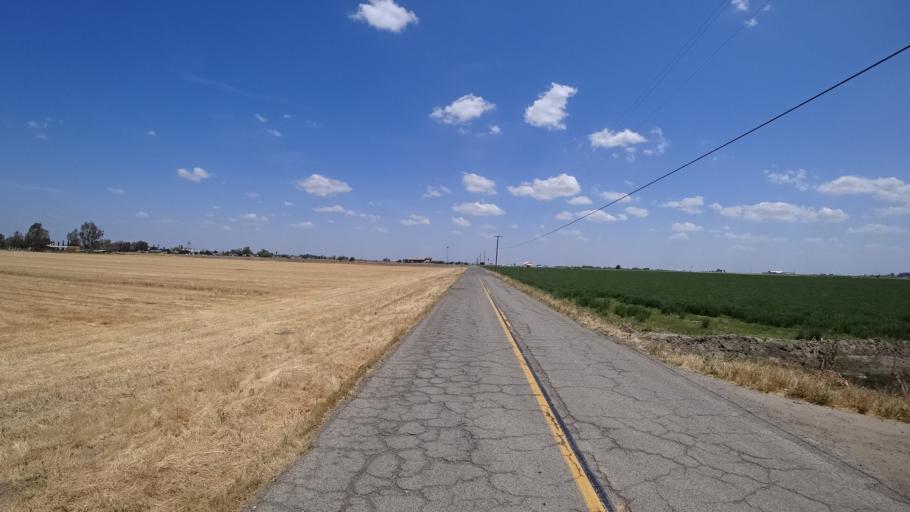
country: US
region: California
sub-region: Kings County
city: Stratford
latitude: 36.1821
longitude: -119.8318
